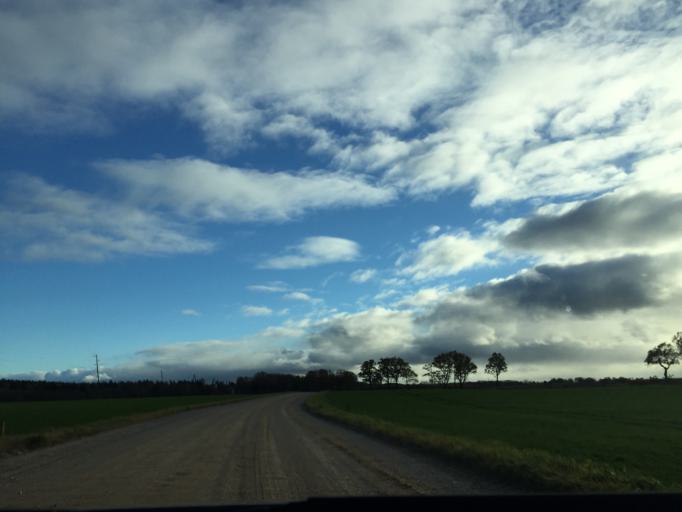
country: LV
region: Kandava
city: Kandava
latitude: 56.9382
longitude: 22.9520
